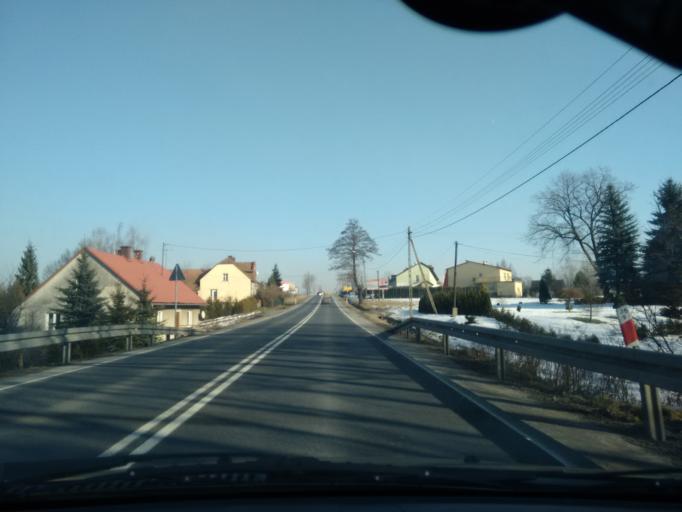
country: PL
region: Lesser Poland Voivodeship
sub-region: Powiat wadowicki
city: Inwald
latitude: 49.8683
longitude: 19.4159
